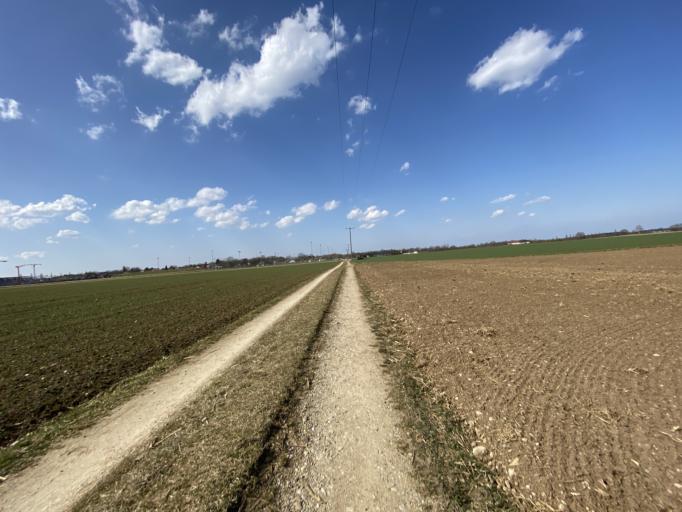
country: DE
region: Bavaria
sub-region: Upper Bavaria
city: Aschheim
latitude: 48.1488
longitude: 11.7012
